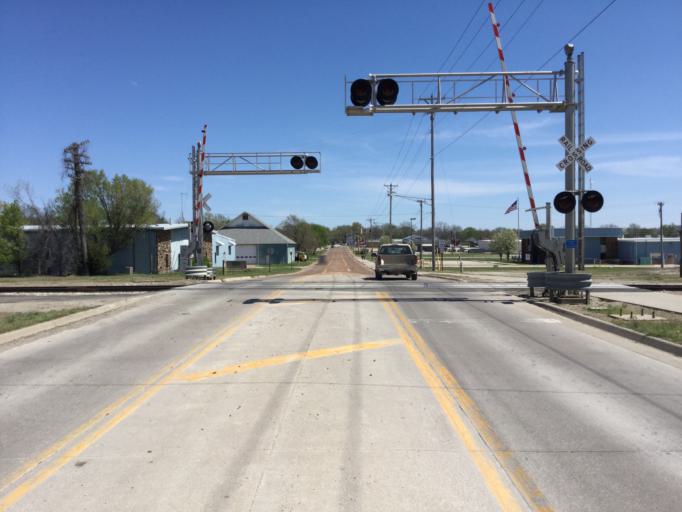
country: US
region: Kansas
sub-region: Neosho County
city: Chanute
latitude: 37.6672
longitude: -95.4573
